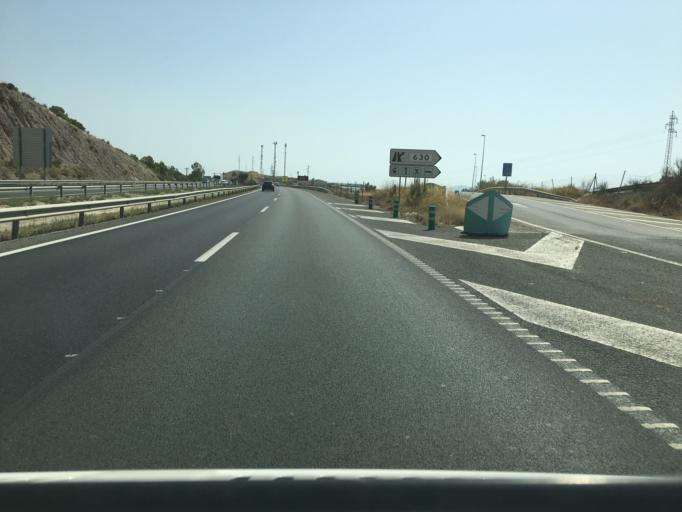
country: ES
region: Murcia
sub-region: Murcia
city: Lorca
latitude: 37.6917
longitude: -1.6696
